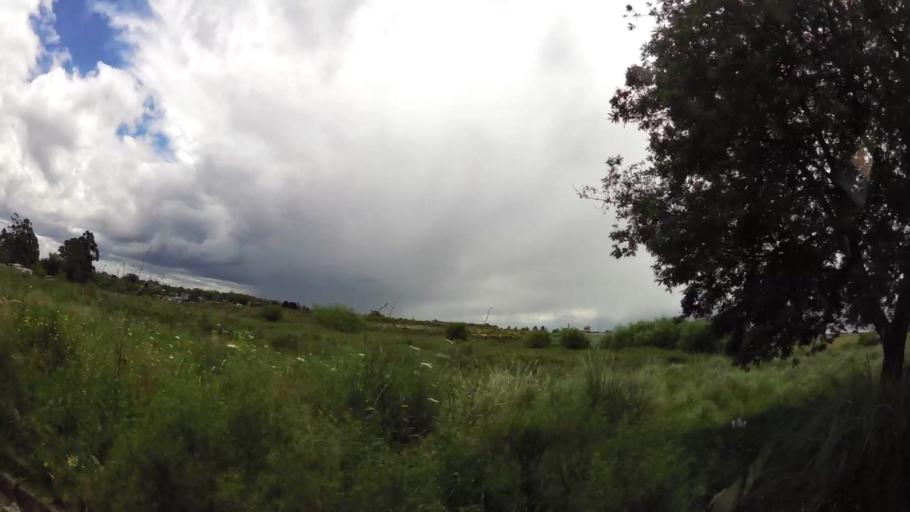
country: UY
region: Canelones
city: La Paz
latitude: -34.8174
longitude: -56.1664
